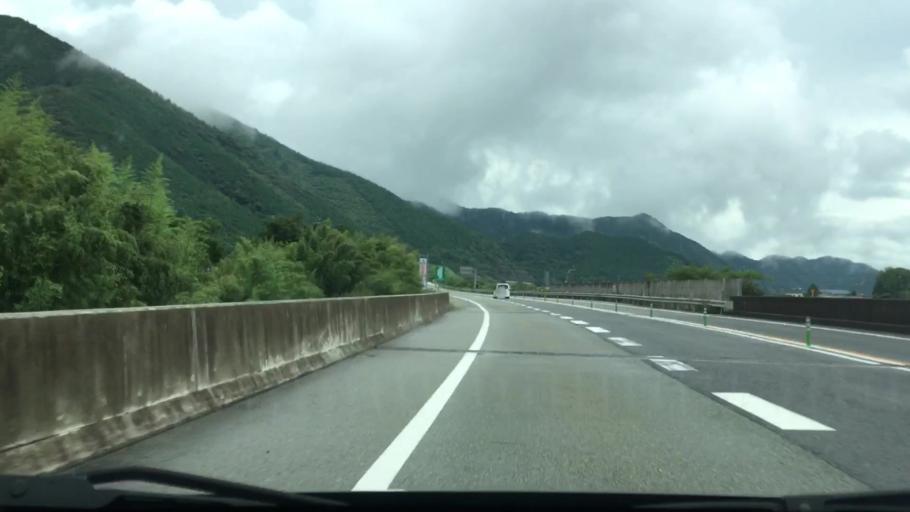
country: JP
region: Hyogo
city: Nishiwaki
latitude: 35.0491
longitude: 134.7643
